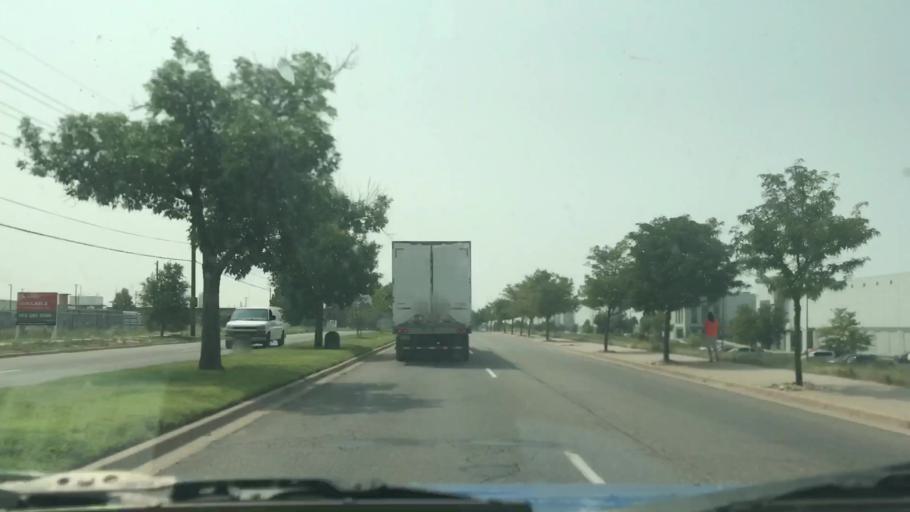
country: US
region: Colorado
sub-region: Adams County
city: Aurora
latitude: 39.7887
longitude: -104.8660
